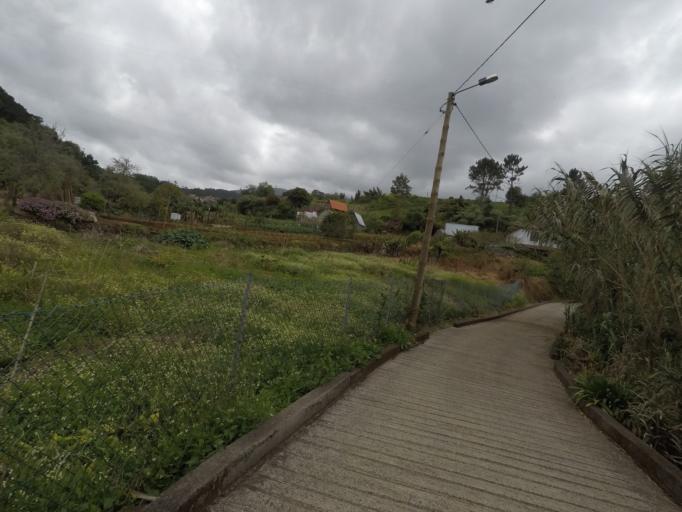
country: PT
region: Madeira
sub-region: Santana
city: Santana
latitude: 32.8019
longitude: -16.8718
